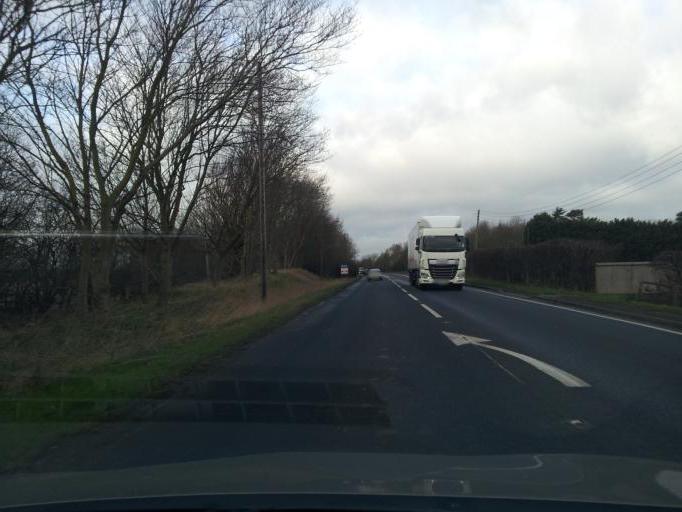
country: GB
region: England
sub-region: Nottinghamshire
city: Bingham
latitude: 52.9415
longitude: -0.8874
